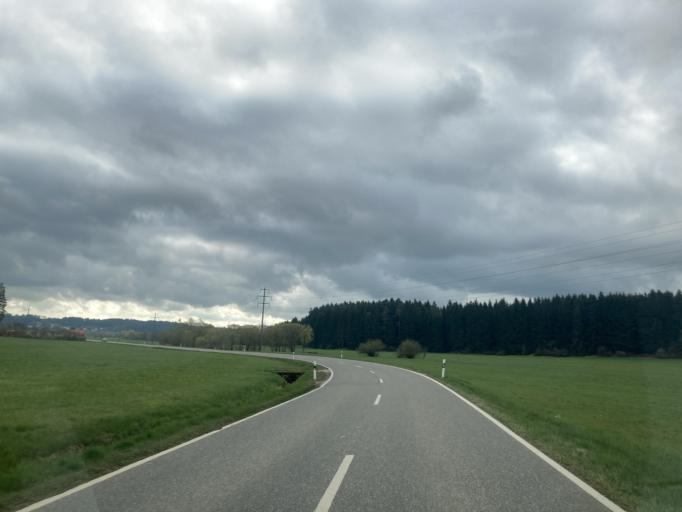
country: DE
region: Baden-Wuerttemberg
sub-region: Freiburg Region
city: Villingen-Schwenningen
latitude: 48.0311
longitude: 8.4367
